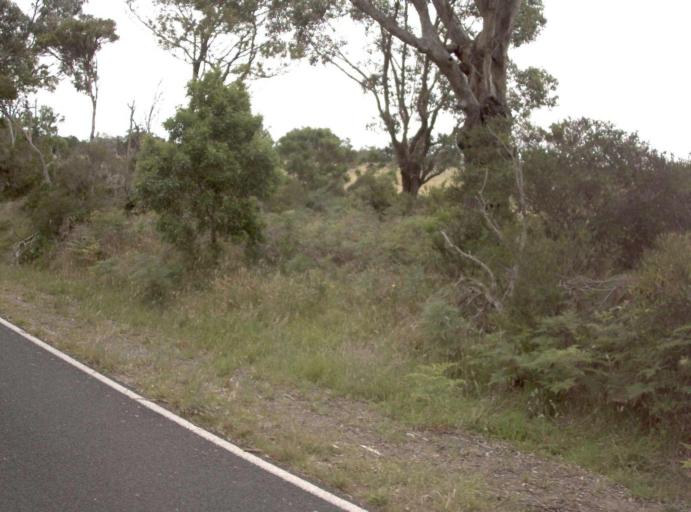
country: AU
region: Victoria
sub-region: Wellington
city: Sale
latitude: -38.5826
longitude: 146.8756
